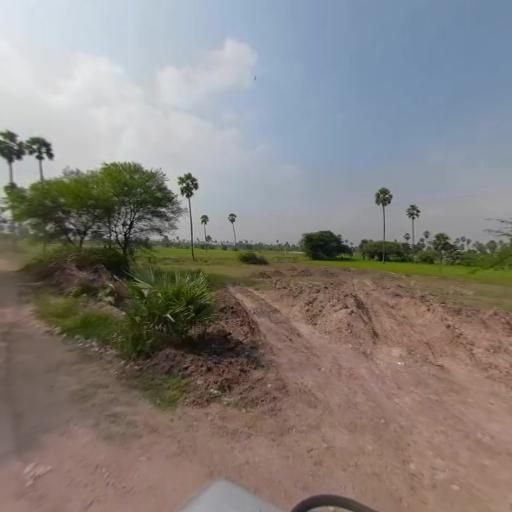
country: IN
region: Telangana
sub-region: Nalgonda
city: Suriapet
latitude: 17.2039
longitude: 79.4853
